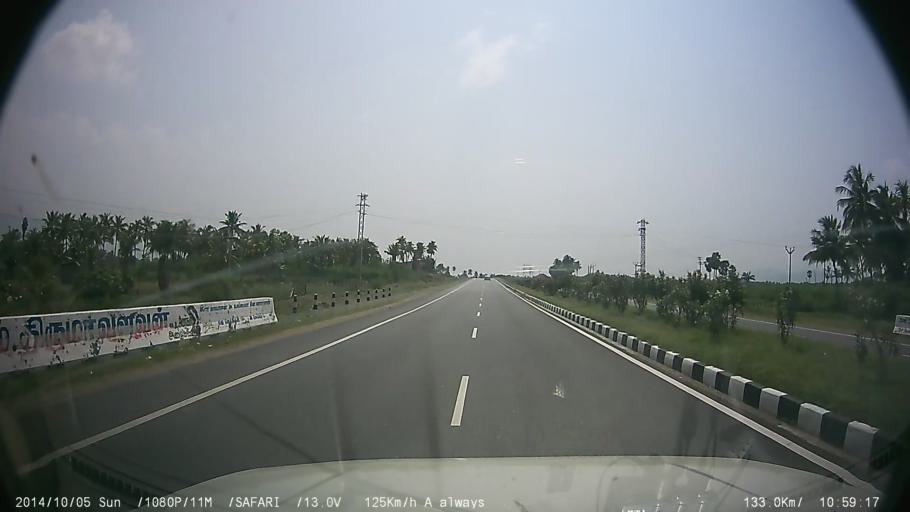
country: IN
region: Tamil Nadu
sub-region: Salem
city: Attur
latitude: 11.6361
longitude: 78.5284
